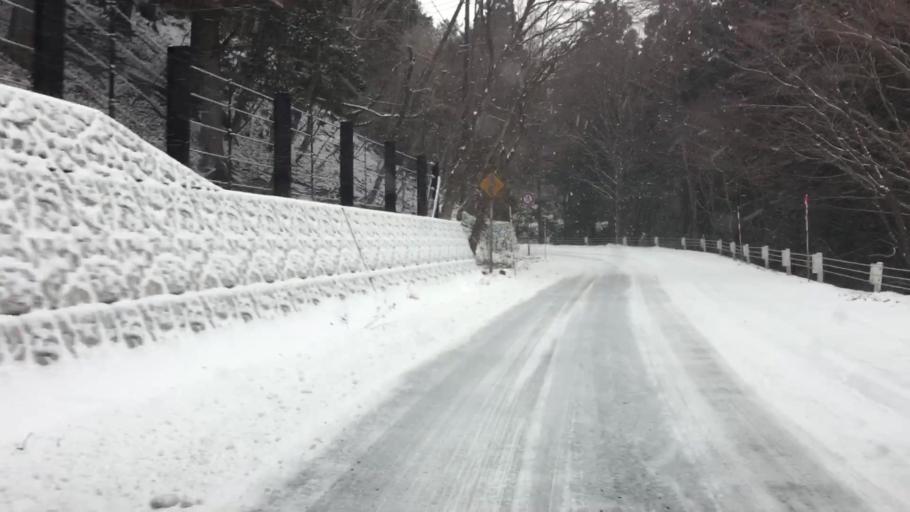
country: JP
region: Tochigi
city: Imaichi
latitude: 36.8733
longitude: 139.7201
